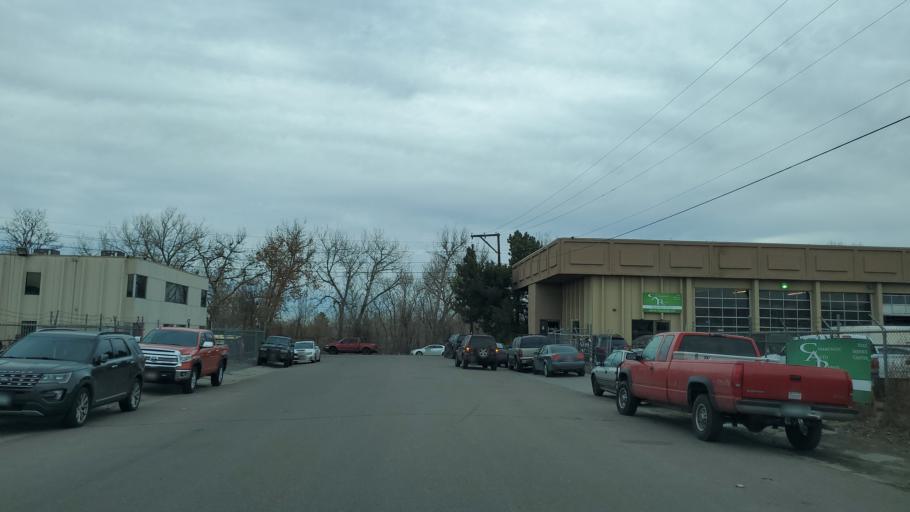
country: US
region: Colorado
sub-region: Denver County
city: Denver
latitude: 39.6978
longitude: -104.9956
